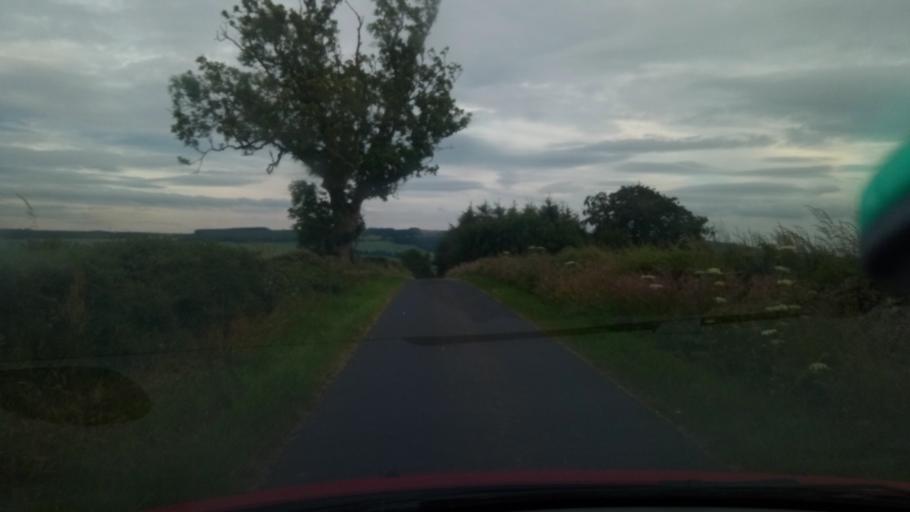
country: GB
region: Scotland
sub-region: The Scottish Borders
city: Saint Boswells
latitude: 55.5033
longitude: -2.6248
